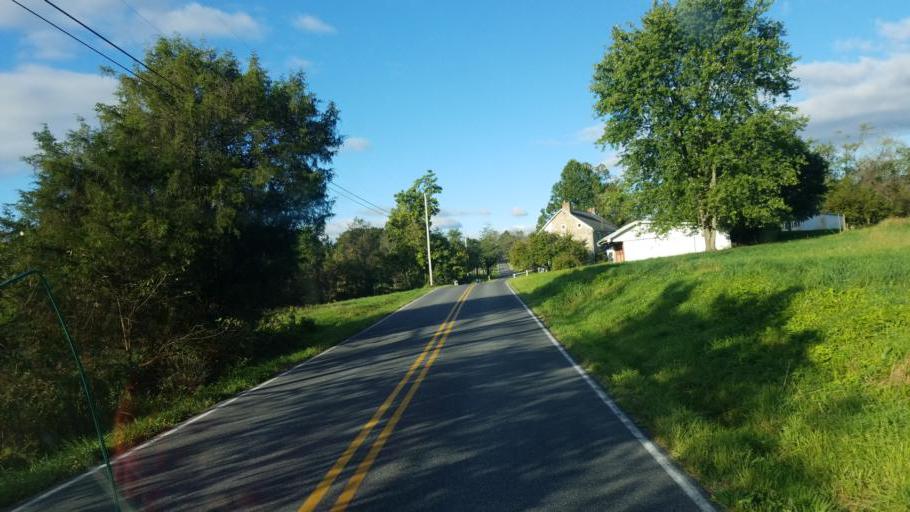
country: US
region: Pennsylvania
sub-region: Adams County
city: Biglerville
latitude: 39.8850
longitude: -77.3048
